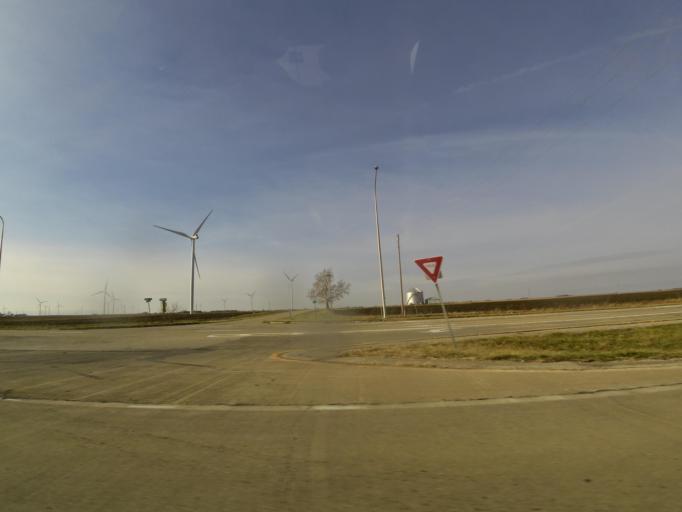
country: US
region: Illinois
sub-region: Macon County
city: Maroa
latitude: 40.0518
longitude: -88.9660
